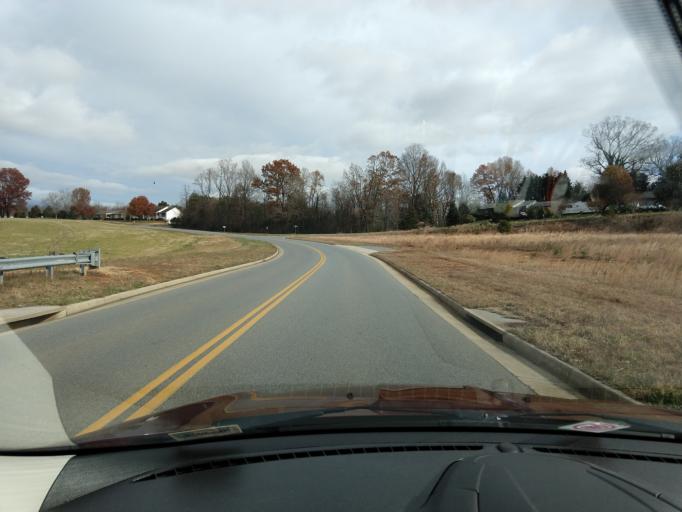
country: US
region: Virginia
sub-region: Franklin County
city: North Shore
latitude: 37.1680
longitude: -79.6364
